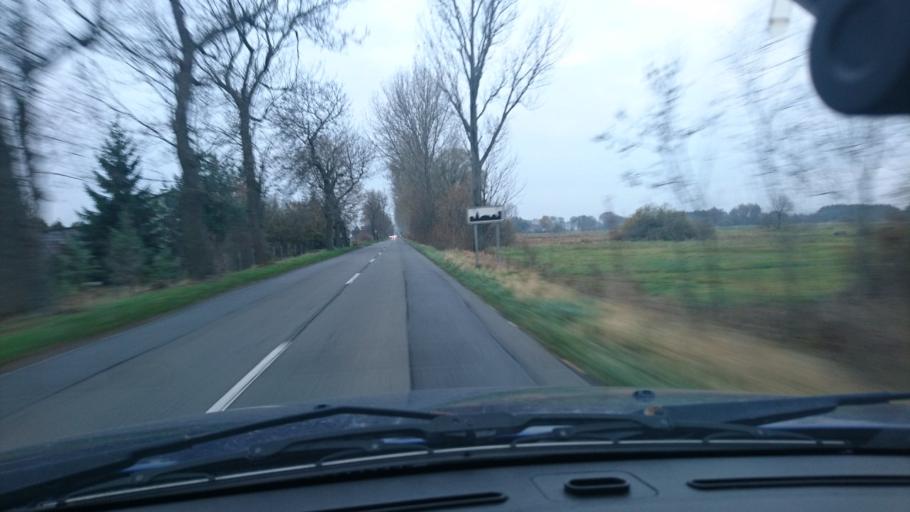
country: PL
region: Greater Poland Voivodeship
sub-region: Powiat ostrowski
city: Odolanow
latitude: 51.5492
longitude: 17.6580
